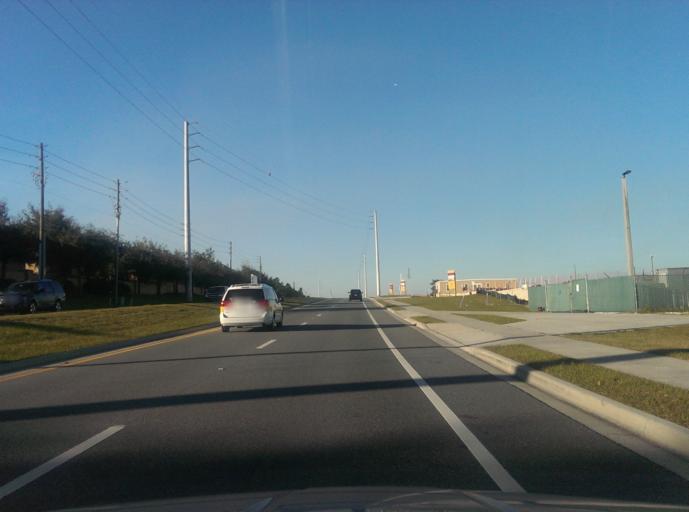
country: US
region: Florida
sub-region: Polk County
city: Citrus Ridge
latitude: 28.3230
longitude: -81.5907
